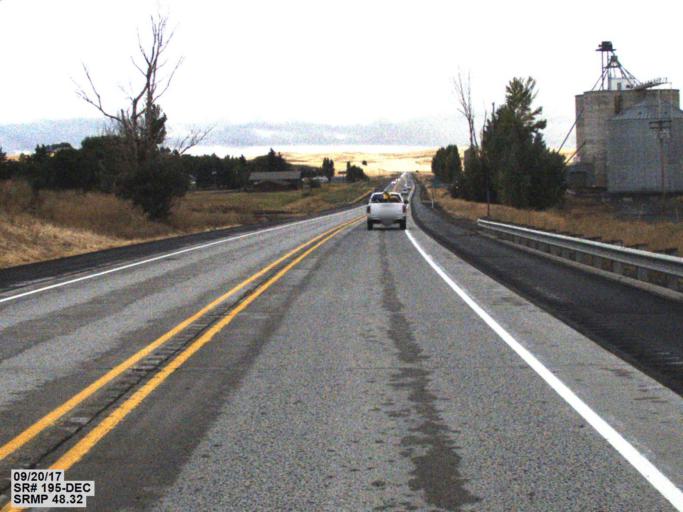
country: US
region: Washington
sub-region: Whitman County
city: Colfax
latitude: 47.0107
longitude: -117.3541
